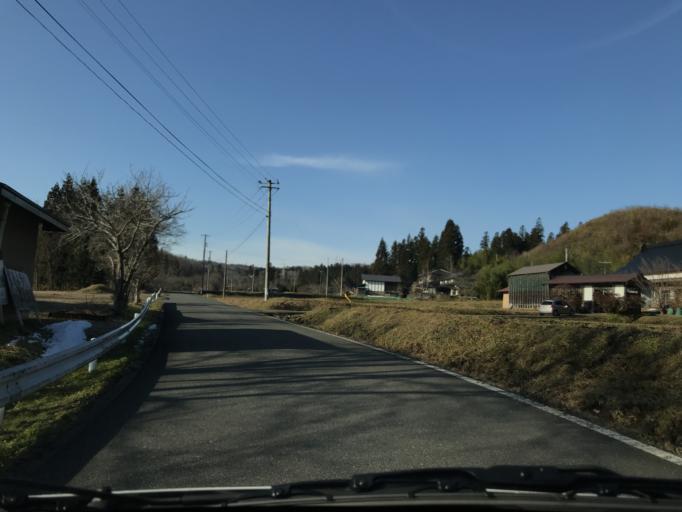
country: JP
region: Iwate
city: Ichinoseki
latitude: 38.9676
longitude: 141.0520
